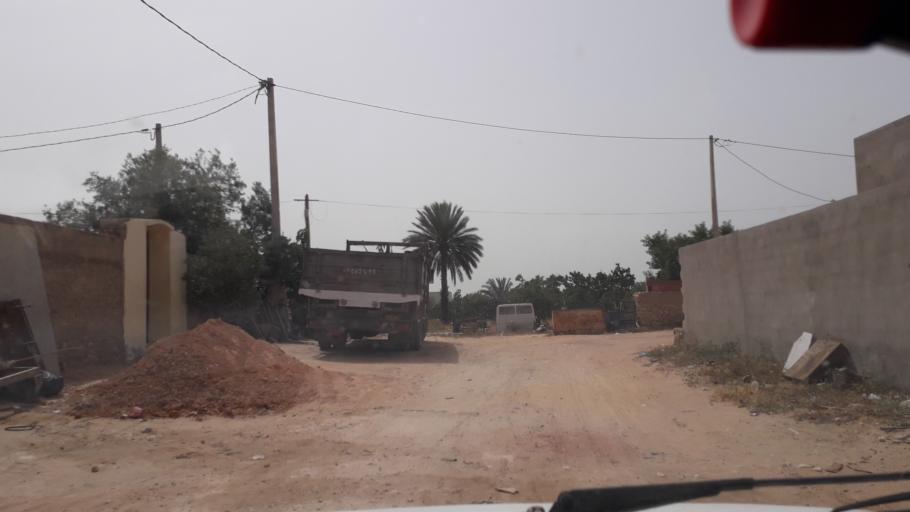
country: TN
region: Safaqis
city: Al Qarmadah
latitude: 34.8075
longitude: 10.7735
